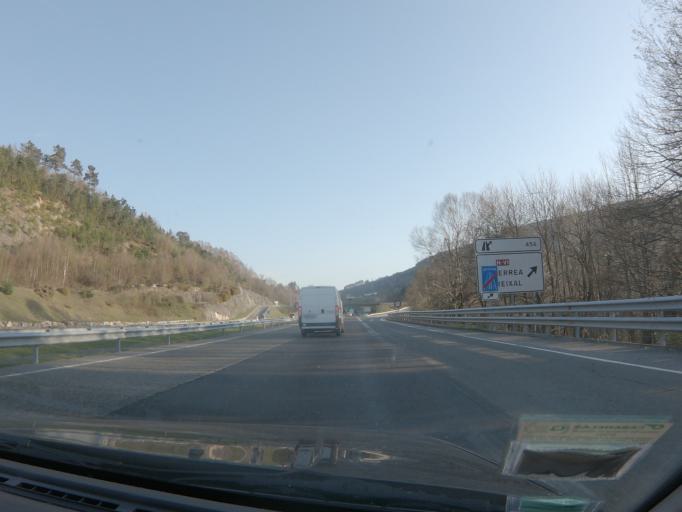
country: ES
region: Galicia
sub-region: Provincia de Lugo
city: Becerrea
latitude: 42.8812
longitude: -7.1768
